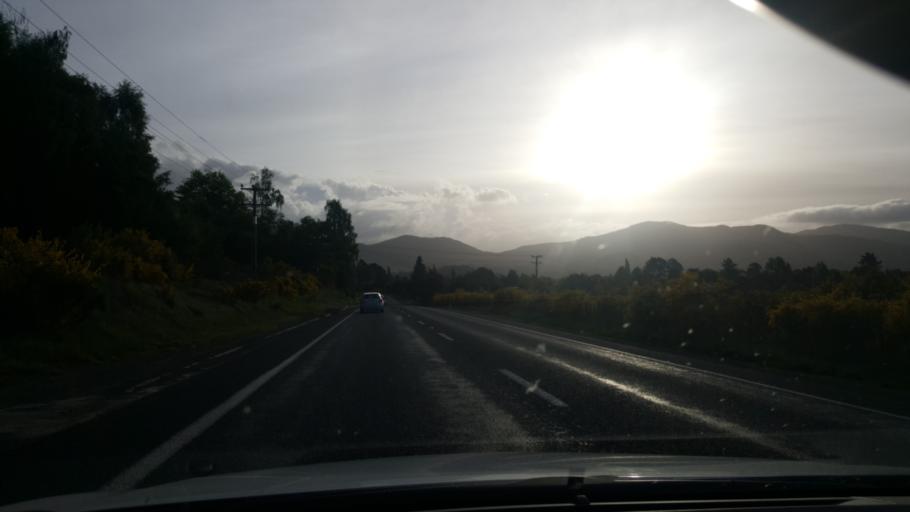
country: NZ
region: Waikato
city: Turangi
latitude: -38.9809
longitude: 175.8241
